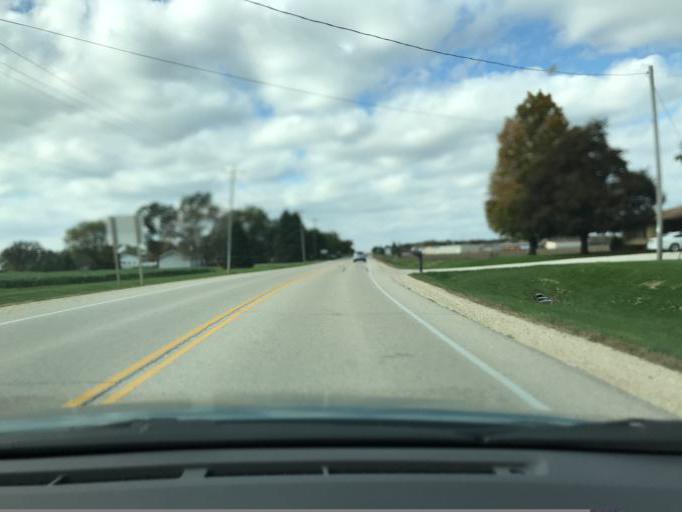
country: US
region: Wisconsin
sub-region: Racine County
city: Burlington
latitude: 42.6644
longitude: -88.2488
